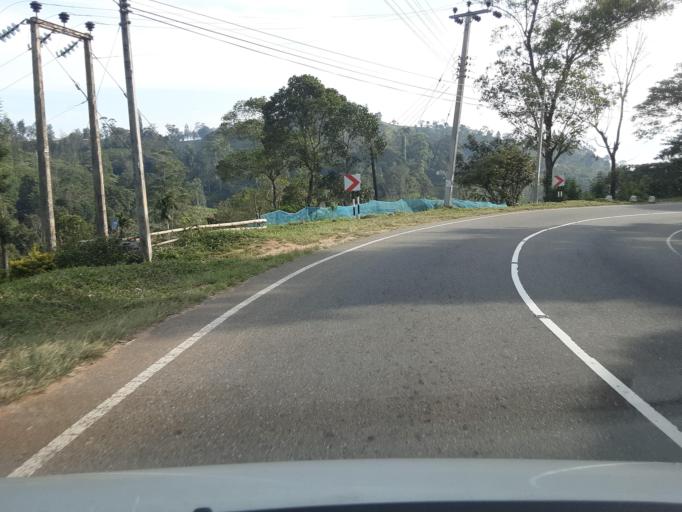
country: LK
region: Uva
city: Badulla
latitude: 6.9391
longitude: 80.9982
